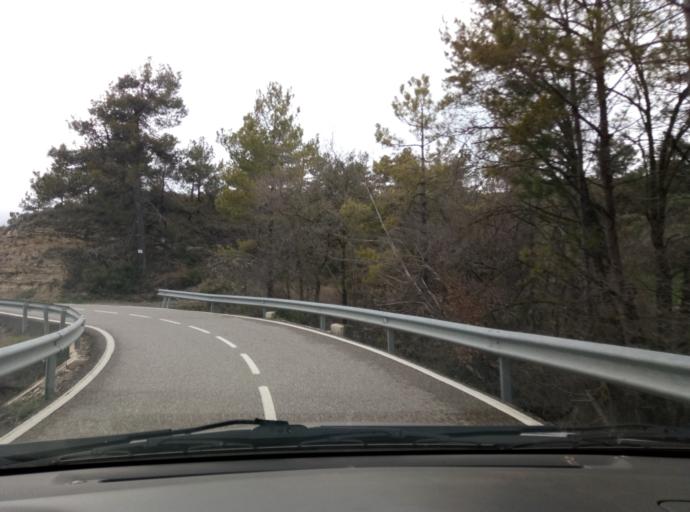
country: ES
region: Catalonia
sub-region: Provincia de Tarragona
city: Conesa
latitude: 41.5436
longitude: 1.3278
